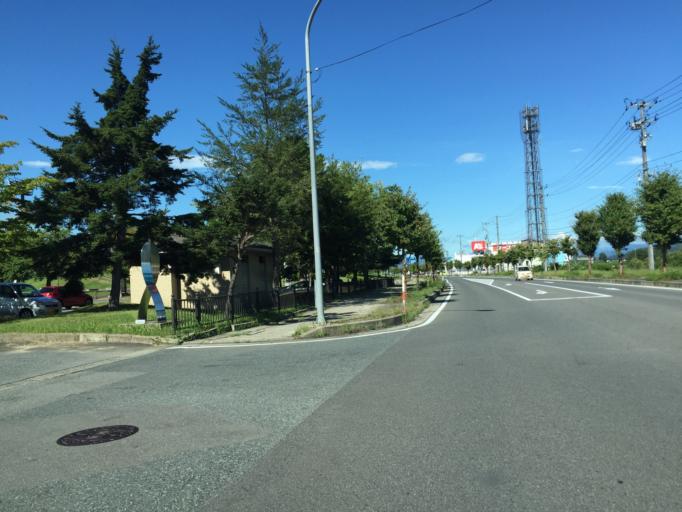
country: JP
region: Yamagata
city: Yonezawa
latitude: 37.9246
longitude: 140.1065
